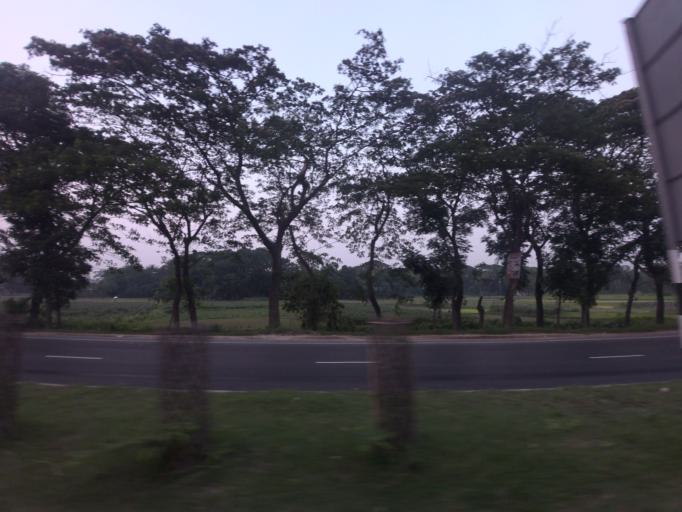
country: BD
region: Chittagong
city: Comilla
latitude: 23.4848
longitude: 91.0224
